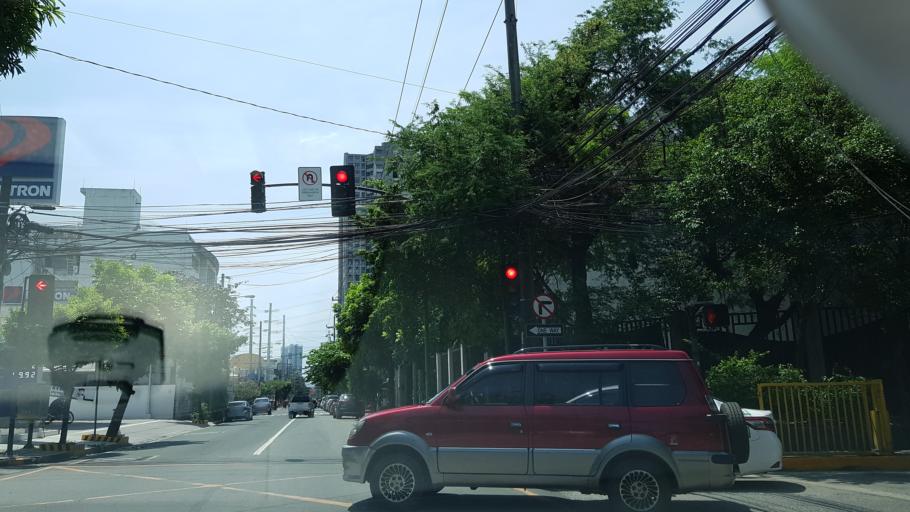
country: PH
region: Metro Manila
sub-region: Makati City
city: Makati City
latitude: 14.5666
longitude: 121.0149
